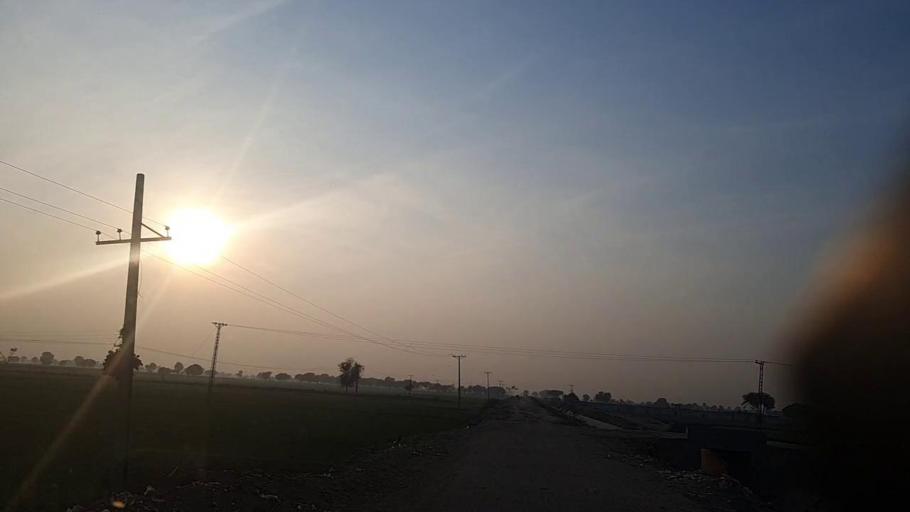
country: PK
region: Sindh
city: Sakrand
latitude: 26.1390
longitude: 68.2216
